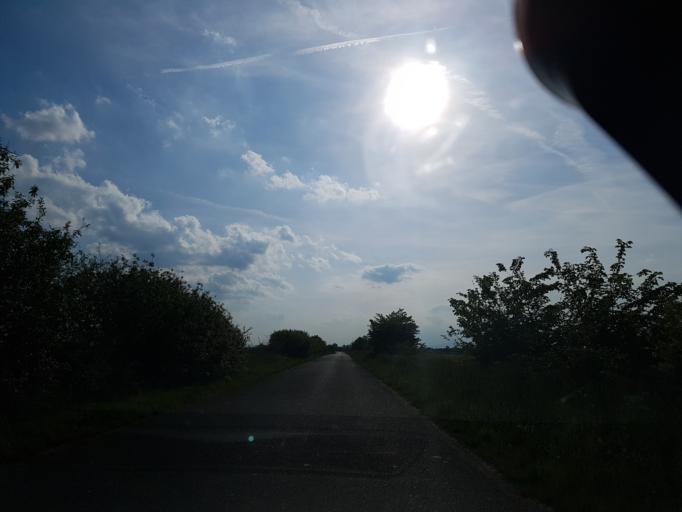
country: PL
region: Lower Silesian Voivodeship
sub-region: Powiat strzelinski
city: Wiazow
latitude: 50.8396
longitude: 17.1943
